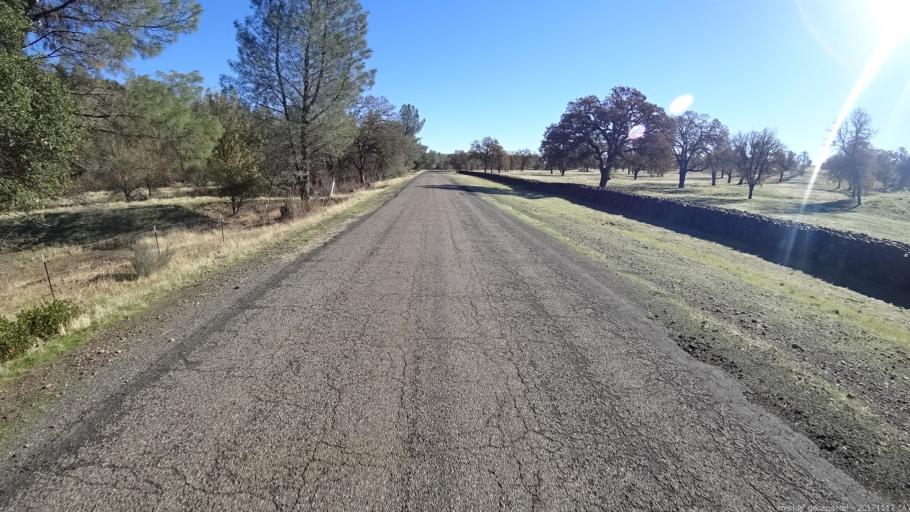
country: US
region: California
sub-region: Shasta County
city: Cottonwood
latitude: 40.4415
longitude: -122.1559
